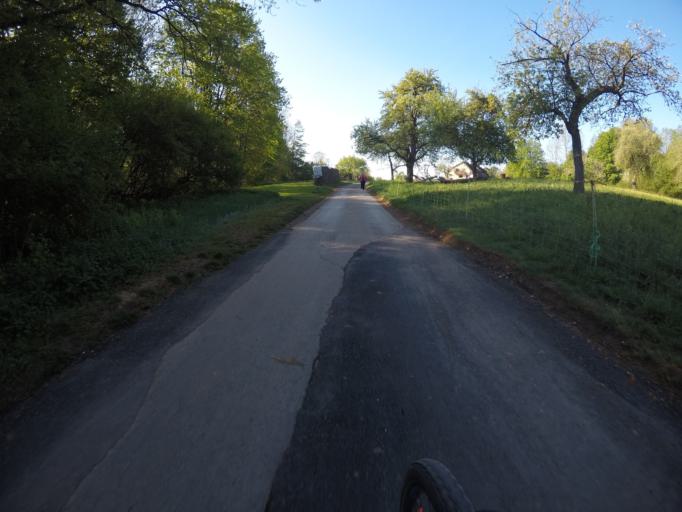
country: DE
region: Baden-Wuerttemberg
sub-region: Regierungsbezirk Stuttgart
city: Neckartailfingen
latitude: 48.6321
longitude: 9.2647
